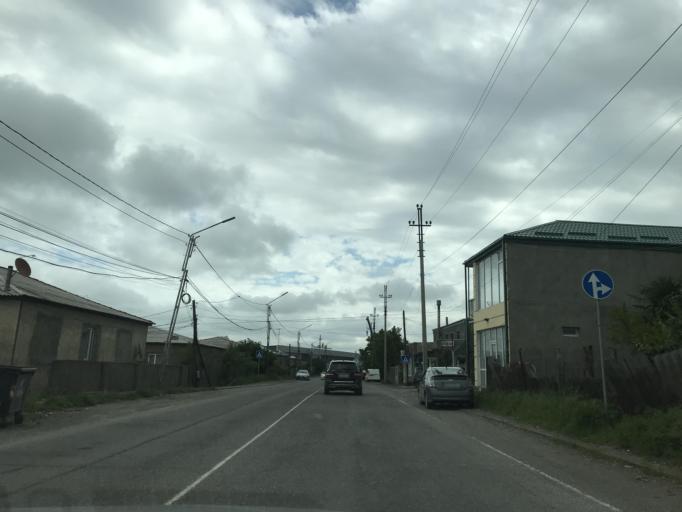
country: GE
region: Kakheti
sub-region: Telavi
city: Telavi
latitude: 41.9224
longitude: 45.4814
